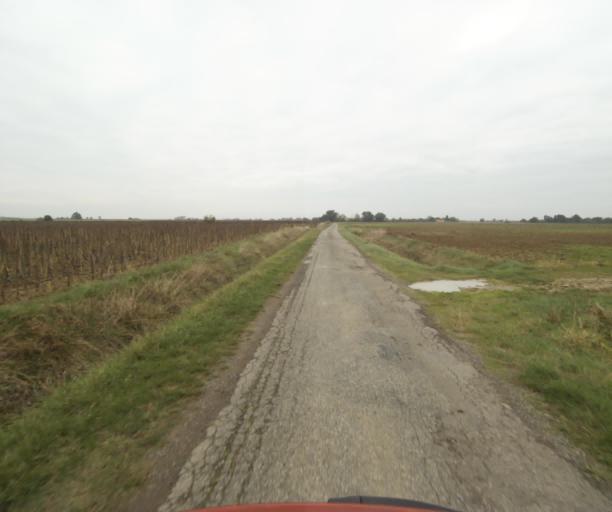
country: FR
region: Midi-Pyrenees
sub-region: Departement de la Haute-Garonne
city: Launac
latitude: 43.8052
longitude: 1.1847
